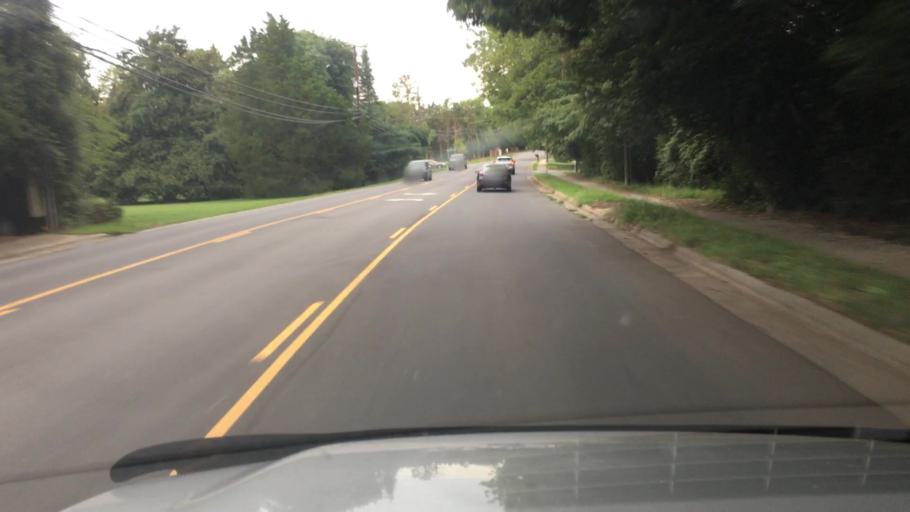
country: US
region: North Carolina
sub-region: Mecklenburg County
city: Pineville
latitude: 35.1224
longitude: -80.8180
